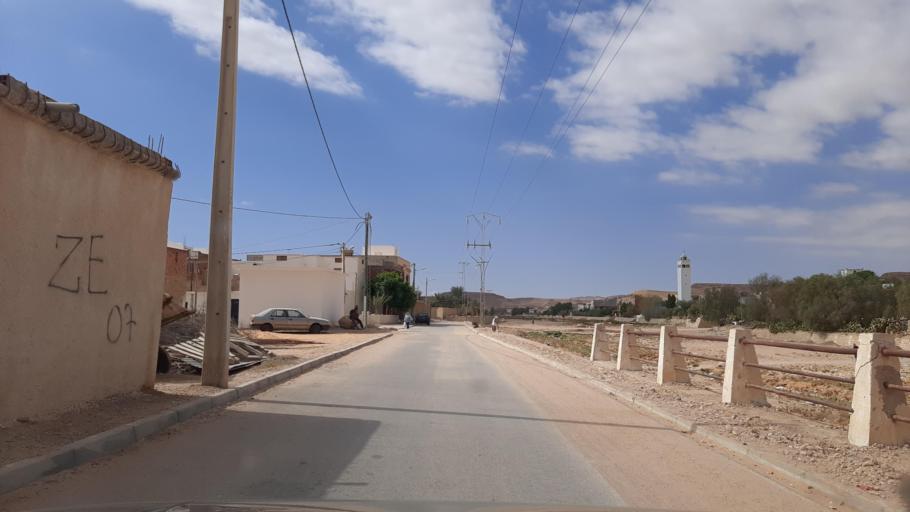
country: TN
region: Tataouine
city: Tataouine
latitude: 32.9320
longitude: 10.4458
